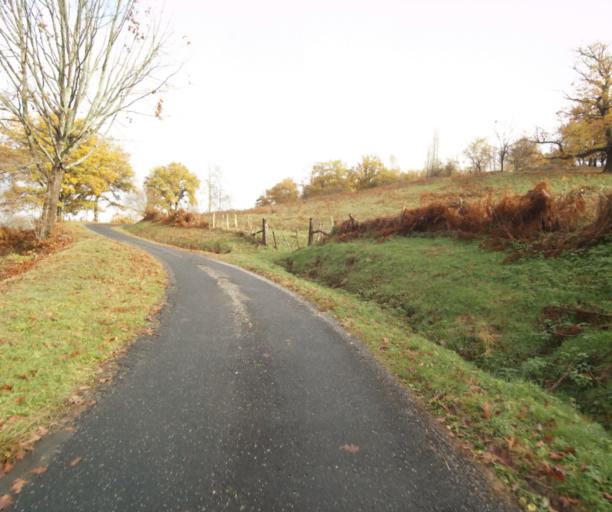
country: FR
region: Limousin
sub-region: Departement de la Correze
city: Sainte-Fereole
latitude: 45.2044
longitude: 1.6314
